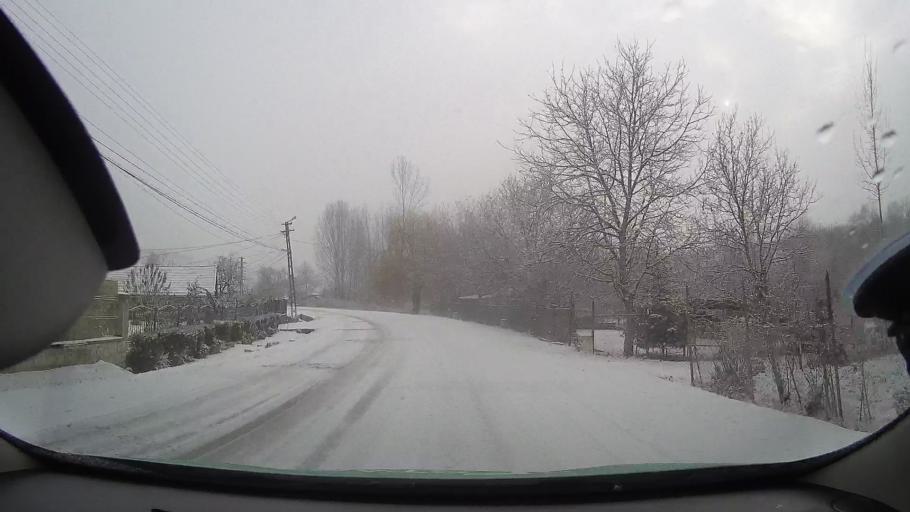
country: RO
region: Alba
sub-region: Comuna Livezile
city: Livezile
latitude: 46.3433
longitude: 23.6592
